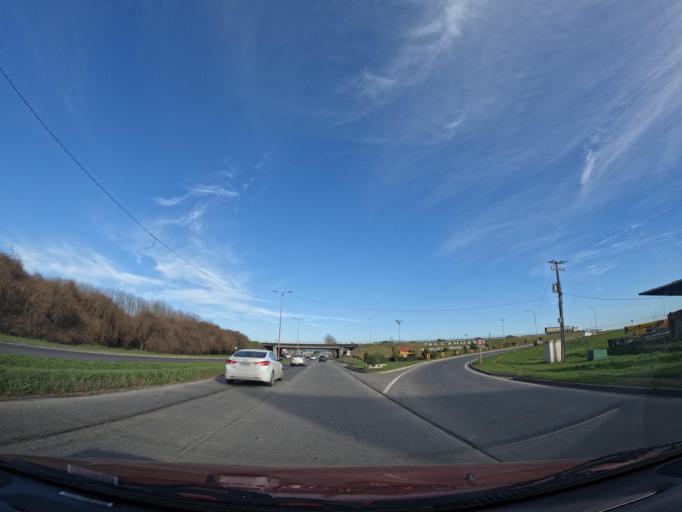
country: CL
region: Biobio
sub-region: Provincia de Concepcion
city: Concepcion
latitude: -36.7838
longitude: -73.0750
